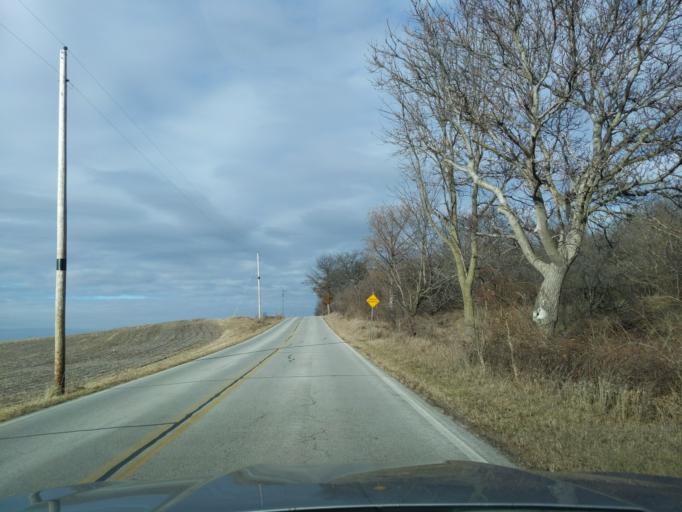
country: US
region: Indiana
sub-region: Tippecanoe County
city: Shadeland
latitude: 40.3381
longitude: -86.9756
